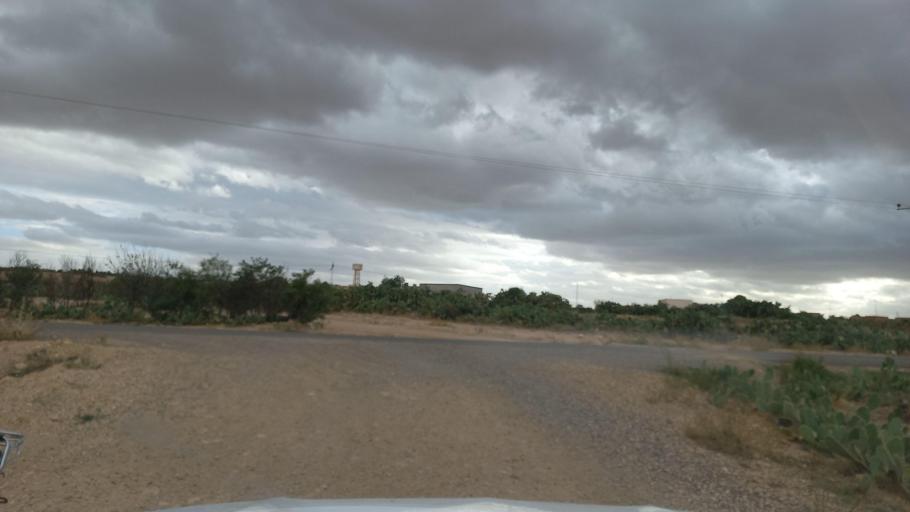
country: TN
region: Al Qasrayn
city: Kasserine
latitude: 35.2776
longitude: 8.9500
